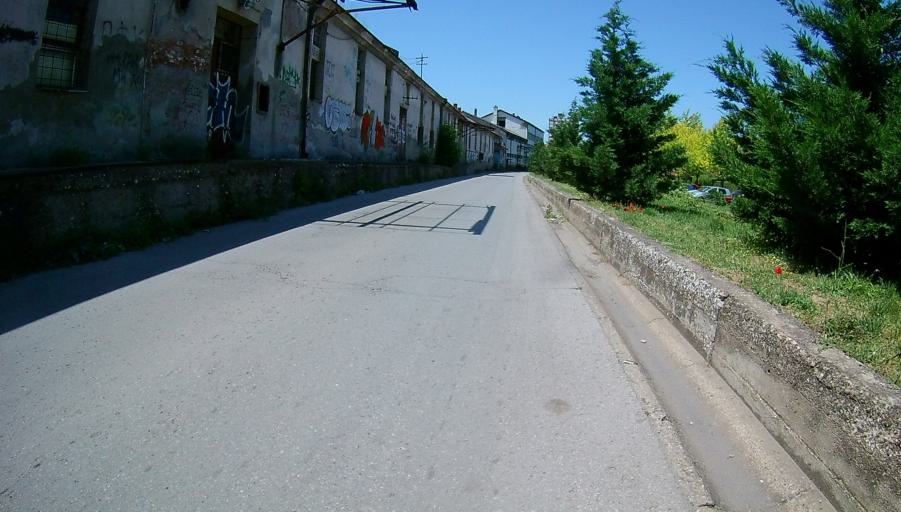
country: RS
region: Central Serbia
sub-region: Nisavski Okrug
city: Nis
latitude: 43.3124
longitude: 21.8925
